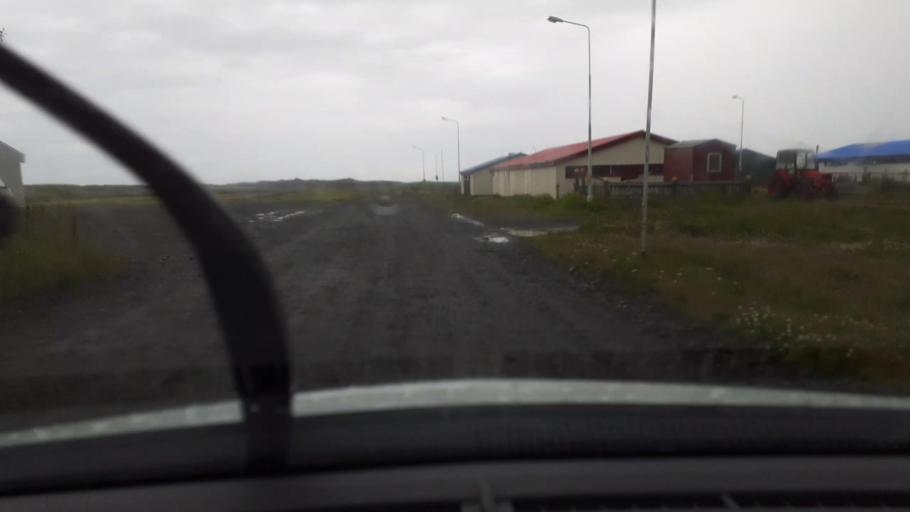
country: IS
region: West
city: Akranes
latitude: 64.3396
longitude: -22.0245
